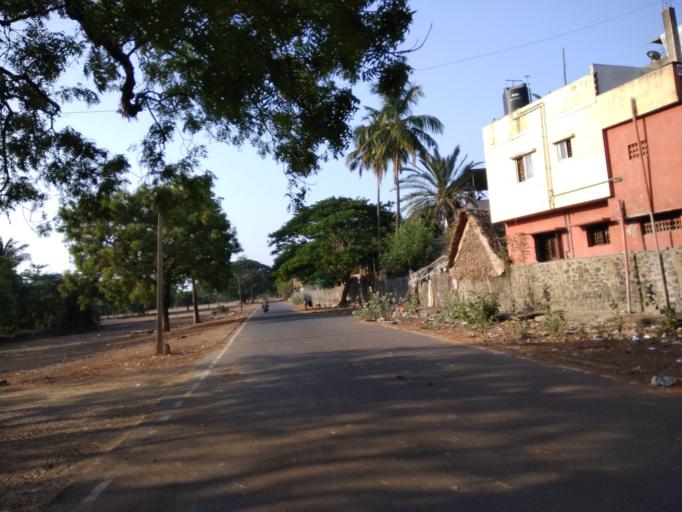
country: IN
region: Tamil Nadu
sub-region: Kancheepuram
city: Saint Thomas Mount
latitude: 13.0168
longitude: 80.1901
